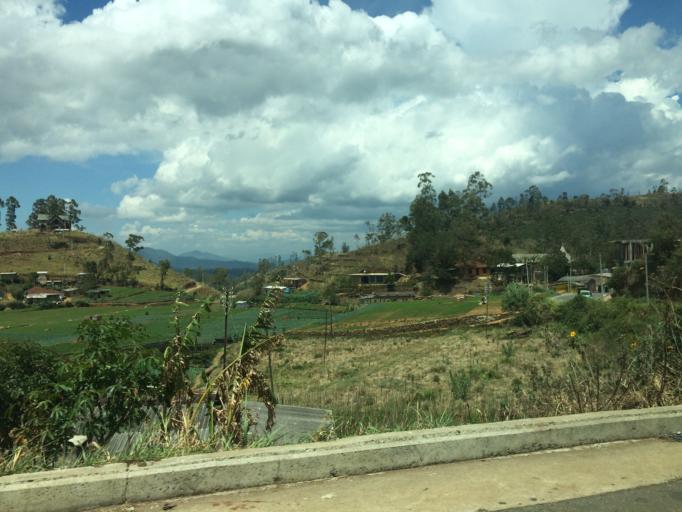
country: LK
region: Central
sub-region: Nuwara Eliya District
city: Nuwara Eliya
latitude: 6.9051
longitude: 80.8454
